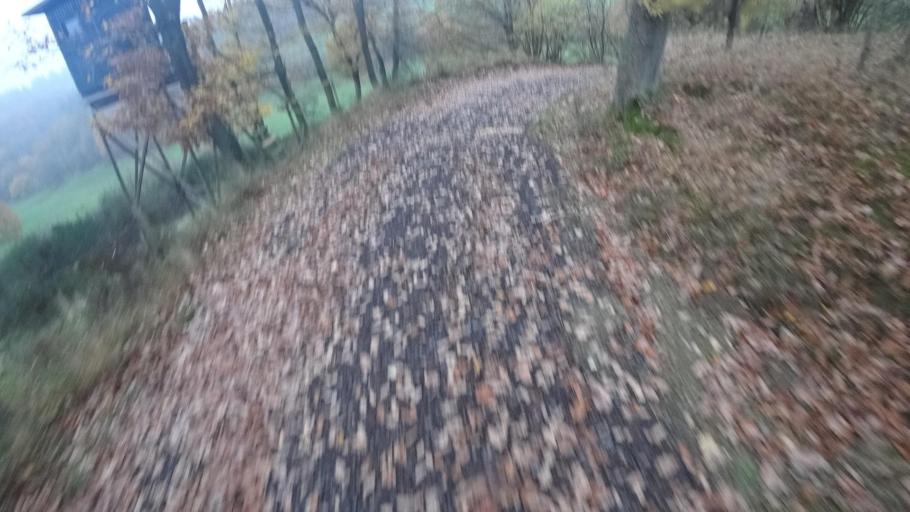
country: DE
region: Rheinland-Pfalz
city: Dernau
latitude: 50.5007
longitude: 7.0676
